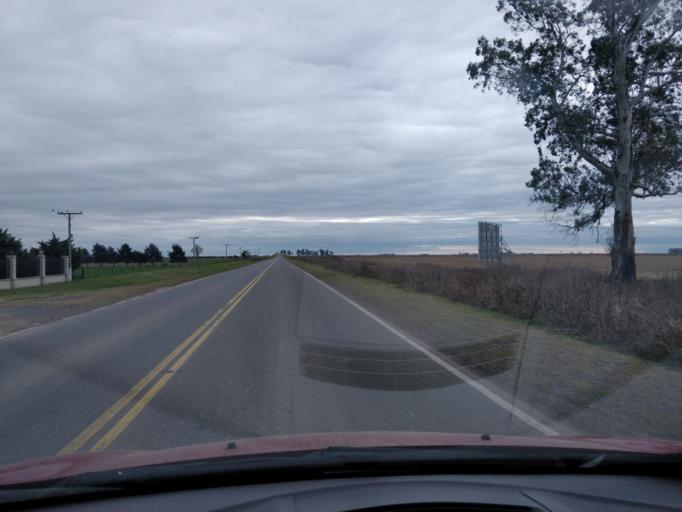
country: AR
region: Cordoba
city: Leones
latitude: -32.6404
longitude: -62.2898
